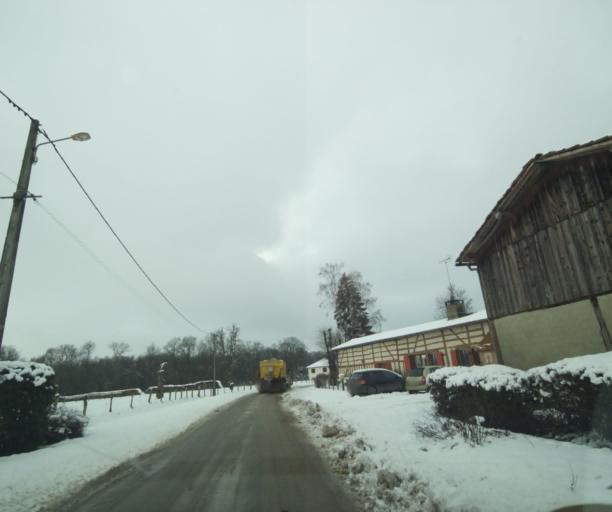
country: FR
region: Champagne-Ardenne
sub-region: Departement de la Haute-Marne
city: Montier-en-Der
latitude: 48.4896
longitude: 4.6931
